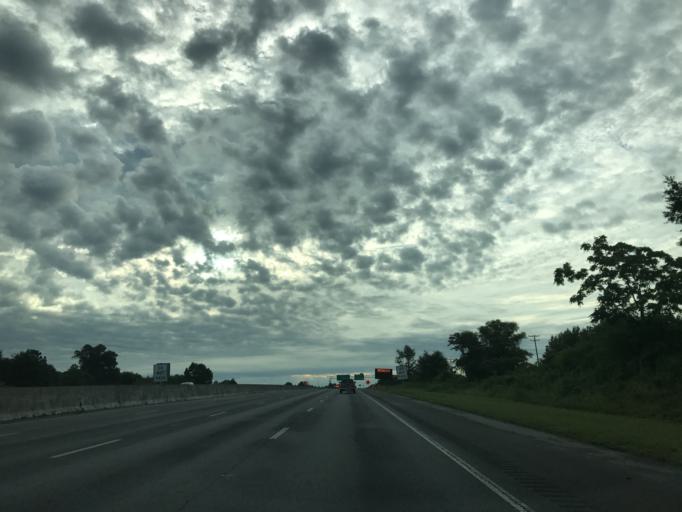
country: US
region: South Carolina
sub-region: Spartanburg County
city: Fairforest
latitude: 34.9631
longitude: -82.0428
